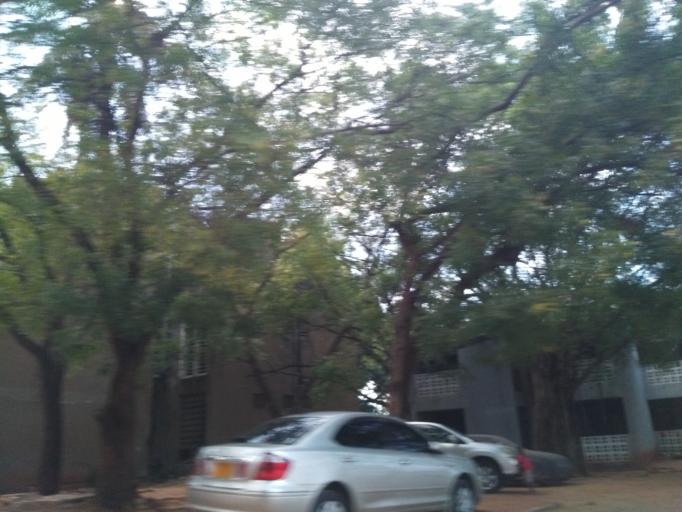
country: TZ
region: Dar es Salaam
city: Magomeni
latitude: -6.7668
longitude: 39.2460
